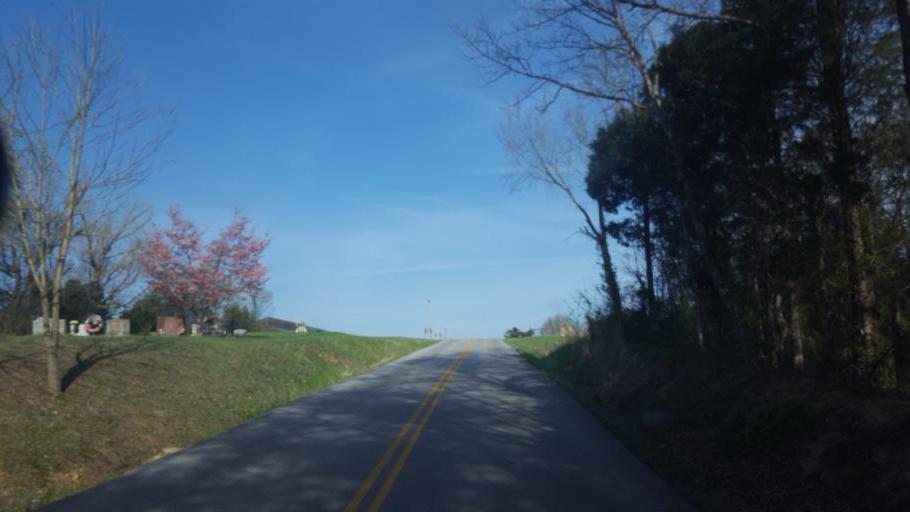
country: US
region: Kentucky
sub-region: Hart County
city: Munfordville
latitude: 37.3175
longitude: -86.0903
